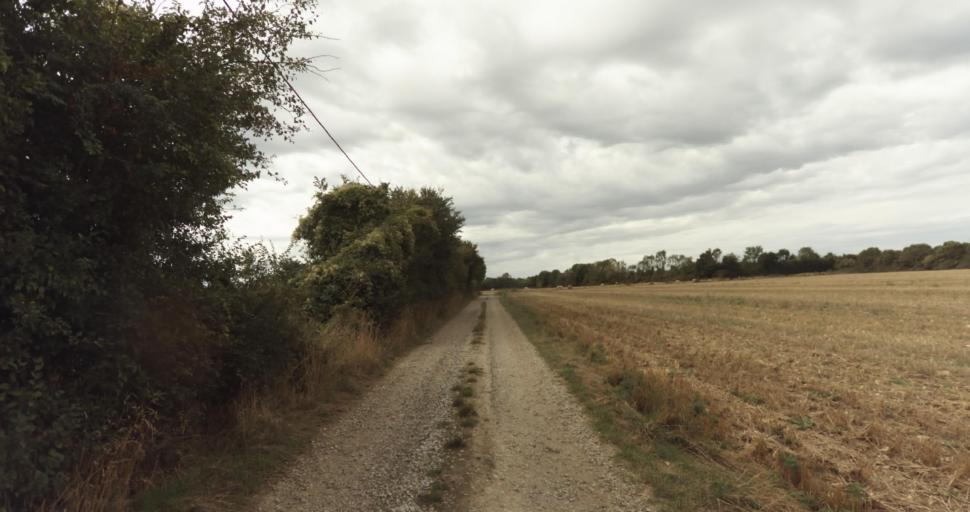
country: FR
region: Lower Normandy
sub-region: Departement de l'Orne
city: Vimoutiers
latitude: 48.9298
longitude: 0.2906
